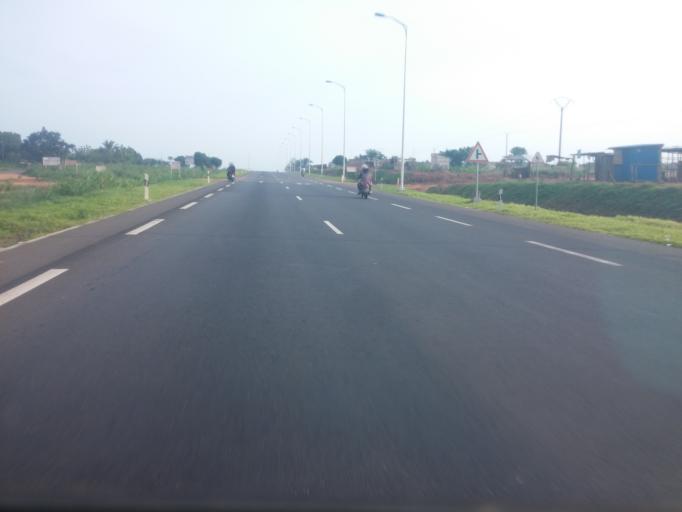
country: TG
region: Maritime
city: Tsevie
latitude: 6.3381
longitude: 1.2157
